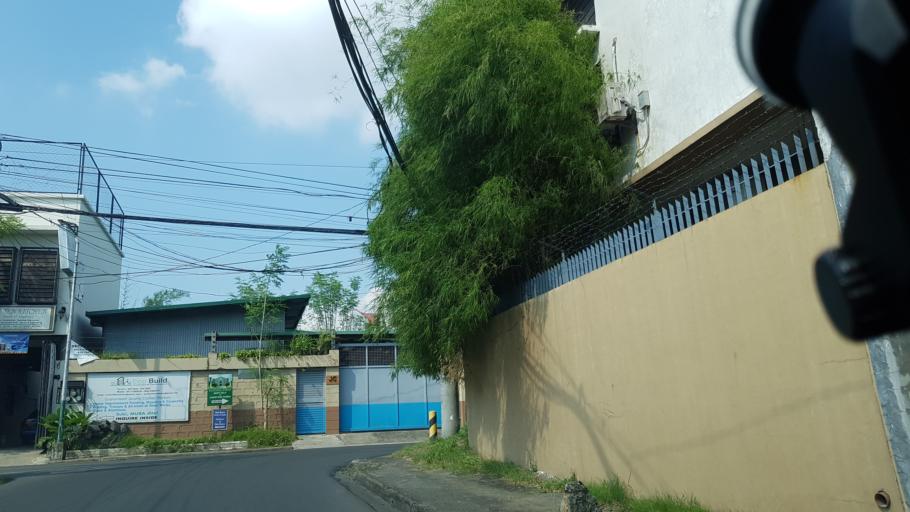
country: PH
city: Sambayanihan People's Village
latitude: 14.4783
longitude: 121.0282
